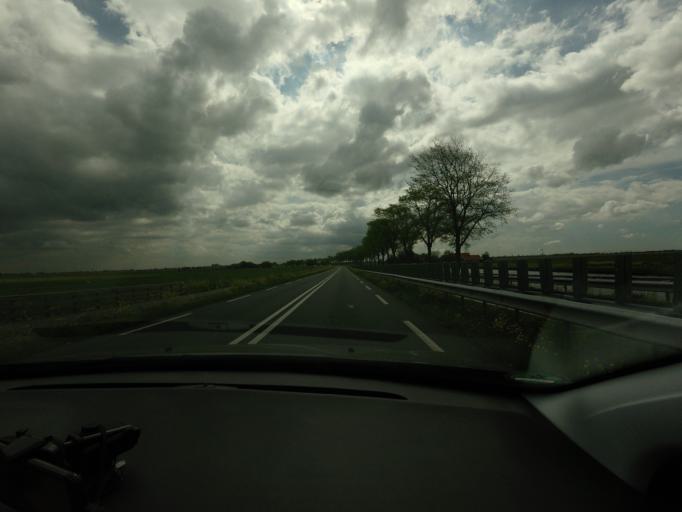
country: NL
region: North Holland
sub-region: Gemeente Landsmeer
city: Landsmeer
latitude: 52.4547
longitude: 4.9496
